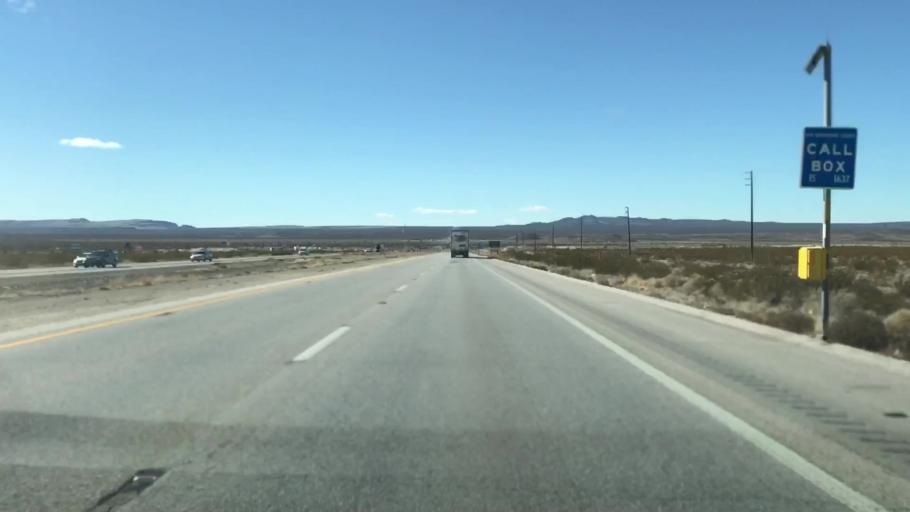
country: US
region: Nevada
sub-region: Clark County
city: Sandy Valley
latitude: 35.4485
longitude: -115.6623
